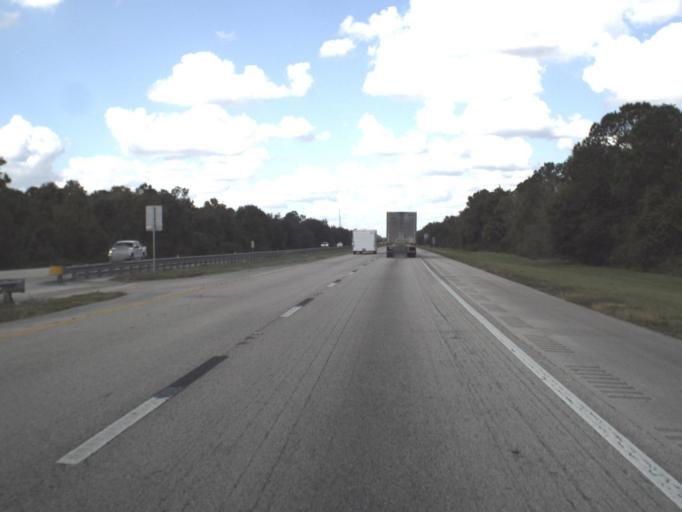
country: US
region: Florida
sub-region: Indian River County
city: Fellsmere
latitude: 27.5744
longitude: -80.8024
